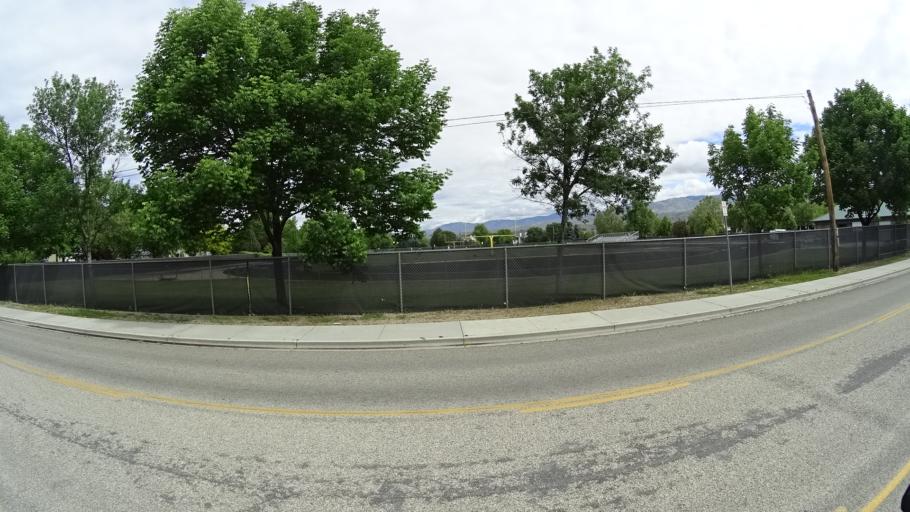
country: US
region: Idaho
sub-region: Ada County
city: Boise
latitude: 43.5787
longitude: -116.1780
